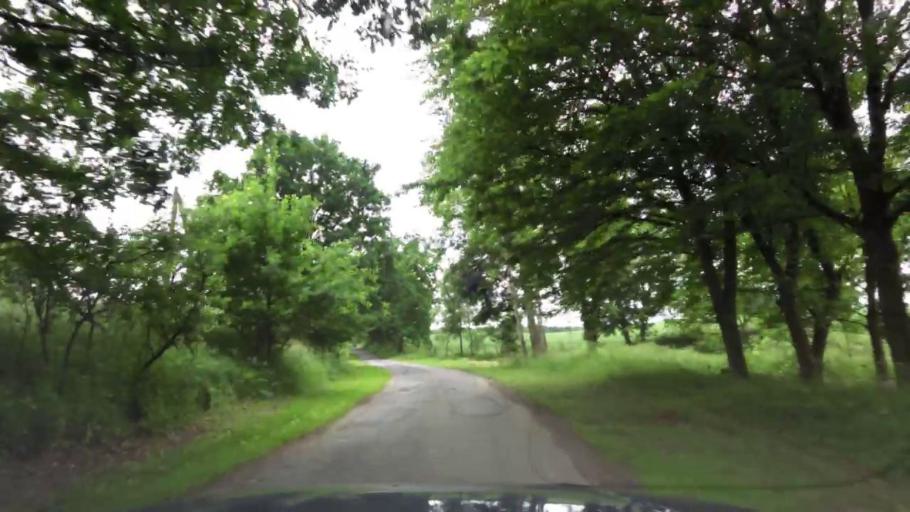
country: PL
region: West Pomeranian Voivodeship
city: Trzcinsko Zdroj
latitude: 52.8795
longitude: 14.5849
